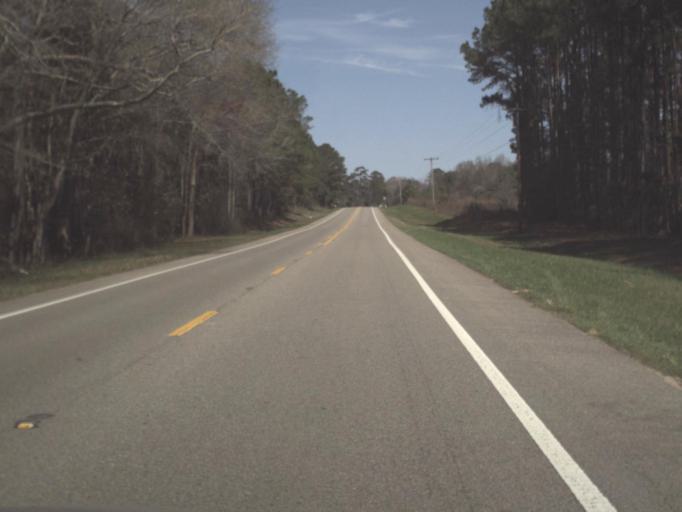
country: US
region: Florida
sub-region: Gadsden County
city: Gretna
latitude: 30.5579
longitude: -84.7534
